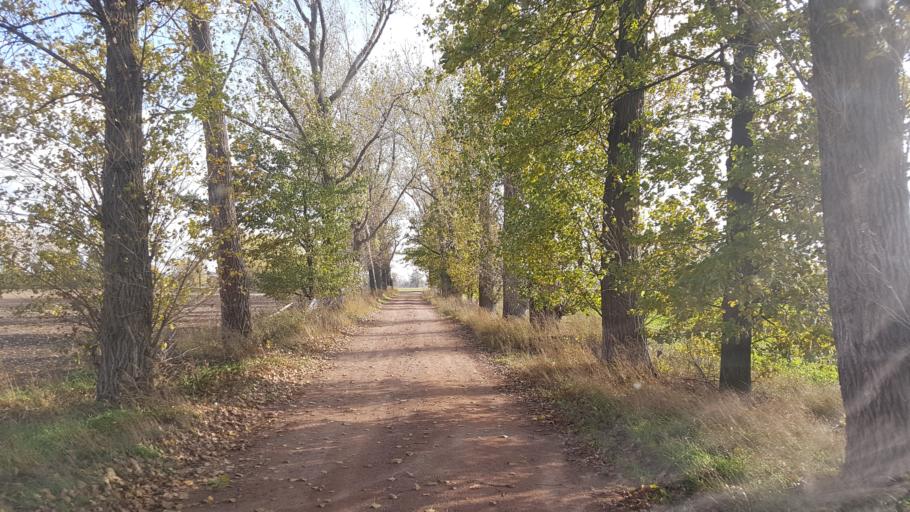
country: DE
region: Brandenburg
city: Schonewalde
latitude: 51.6906
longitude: 13.5747
